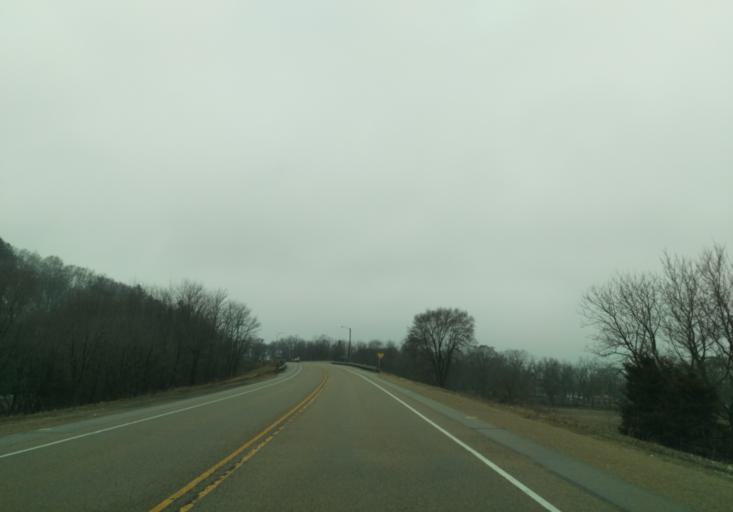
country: US
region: Wisconsin
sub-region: Dane County
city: Mazomanie
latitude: 43.1724
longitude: -89.7854
